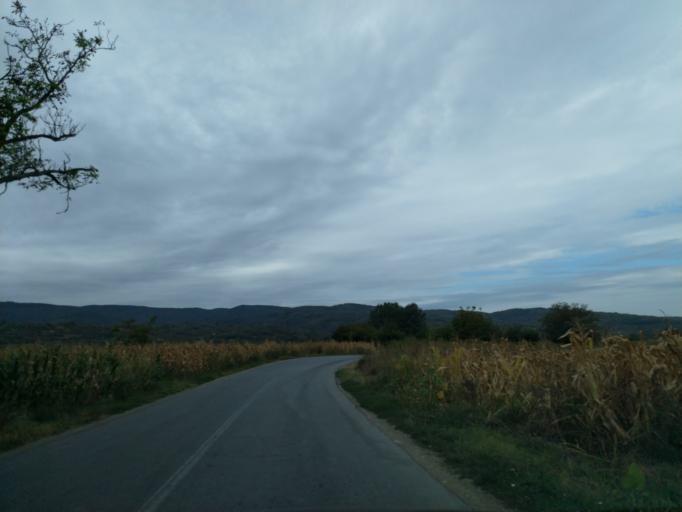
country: RS
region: Central Serbia
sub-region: Pomoravski Okrug
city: Paracin
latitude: 43.8312
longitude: 21.3337
